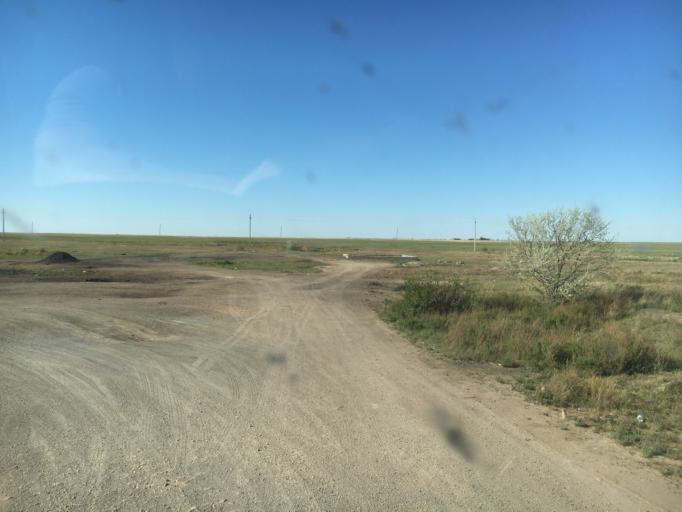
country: RU
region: Orenburg
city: Dombarovskiy
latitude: 50.1071
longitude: 59.3448
